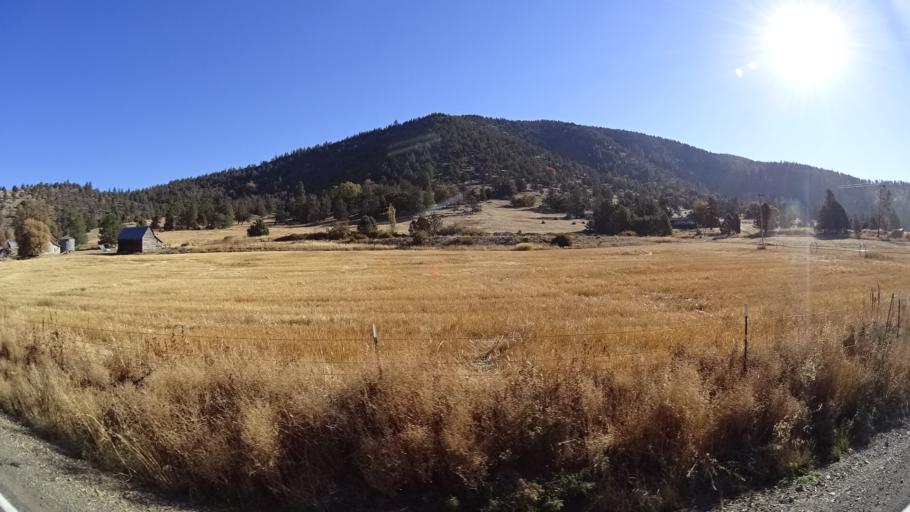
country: US
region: California
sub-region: Siskiyou County
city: Yreka
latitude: 41.5235
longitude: -122.8419
